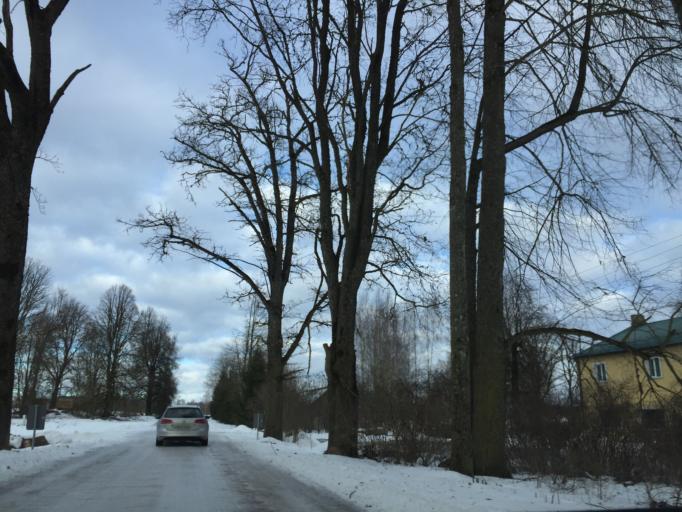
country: LV
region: Lielvarde
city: Lielvarde
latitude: 56.5650
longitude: 24.7342
